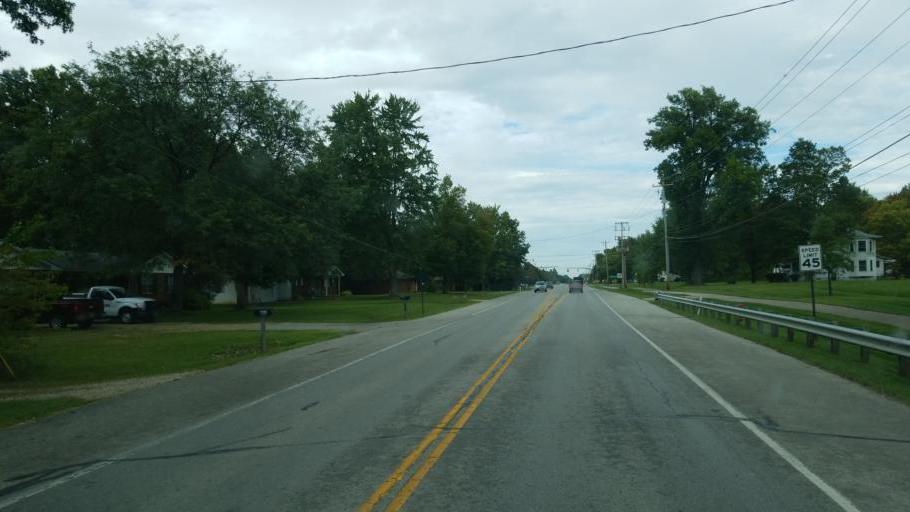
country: US
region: Ohio
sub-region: Franklin County
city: New Albany
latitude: 40.0957
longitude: -82.8125
